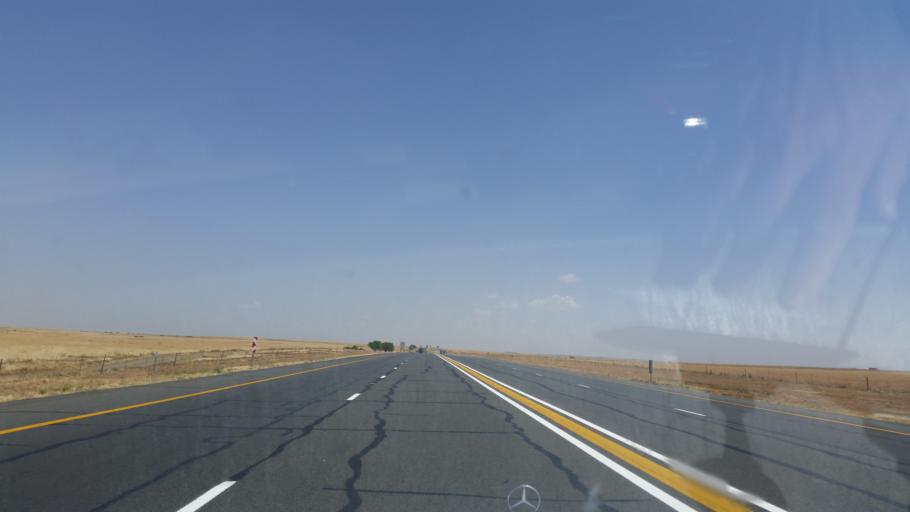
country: ZA
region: Orange Free State
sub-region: Lejweleputswa District Municipality
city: Brandfort
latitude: -28.8756
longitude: 26.5105
